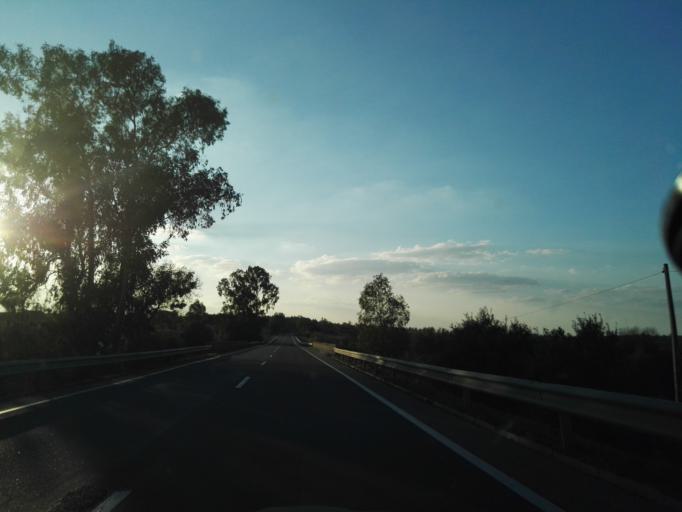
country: PT
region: Evora
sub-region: Arraiolos
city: Arraiolos
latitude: 38.8808
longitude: -7.9902
